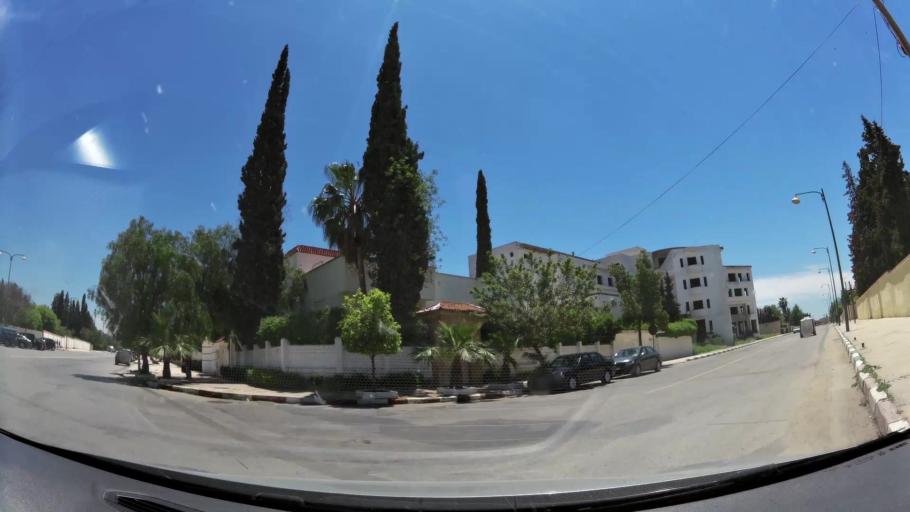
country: MA
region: Meknes-Tafilalet
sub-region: Meknes
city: Meknes
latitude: 33.9057
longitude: -5.5601
